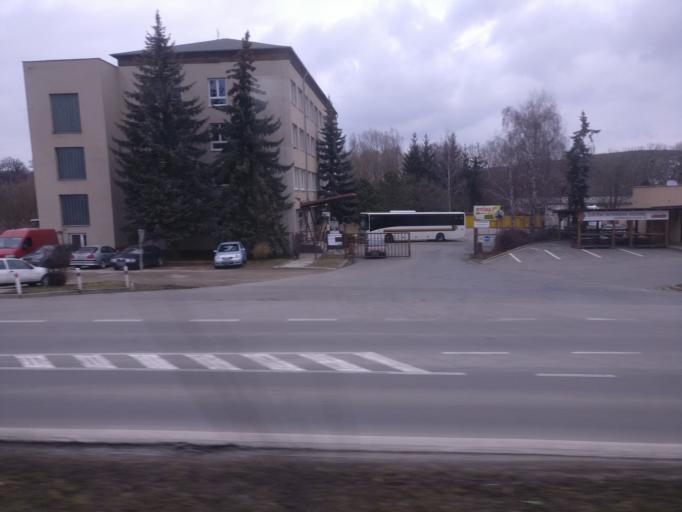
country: CZ
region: South Moravian
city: Zastavka
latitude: 49.1839
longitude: 16.3709
